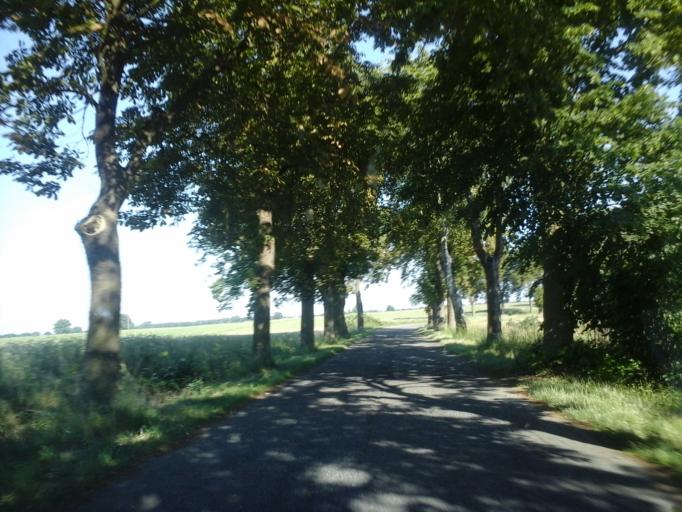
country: PL
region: West Pomeranian Voivodeship
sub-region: Powiat goleniowski
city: Nowogard
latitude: 53.7250
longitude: 15.1995
